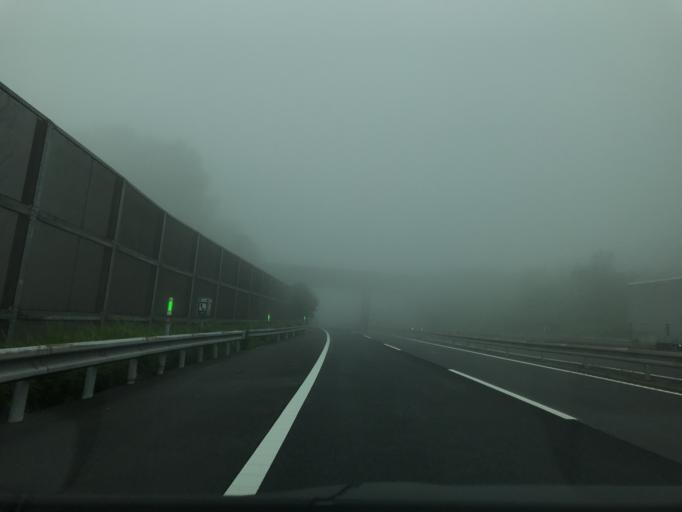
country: JP
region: Oita
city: Hiji
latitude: 33.3655
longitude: 131.4533
